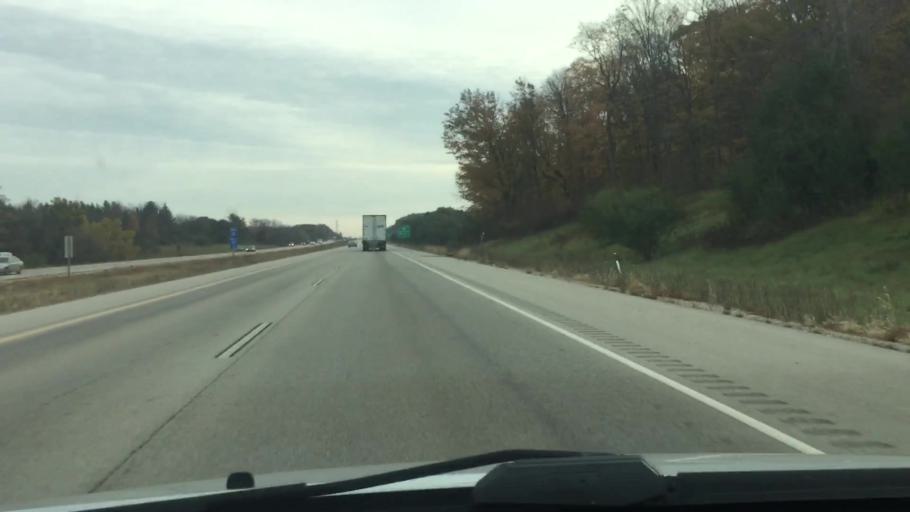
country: US
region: Wisconsin
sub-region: Waukesha County
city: Big Bend
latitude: 42.9029
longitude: -88.2452
